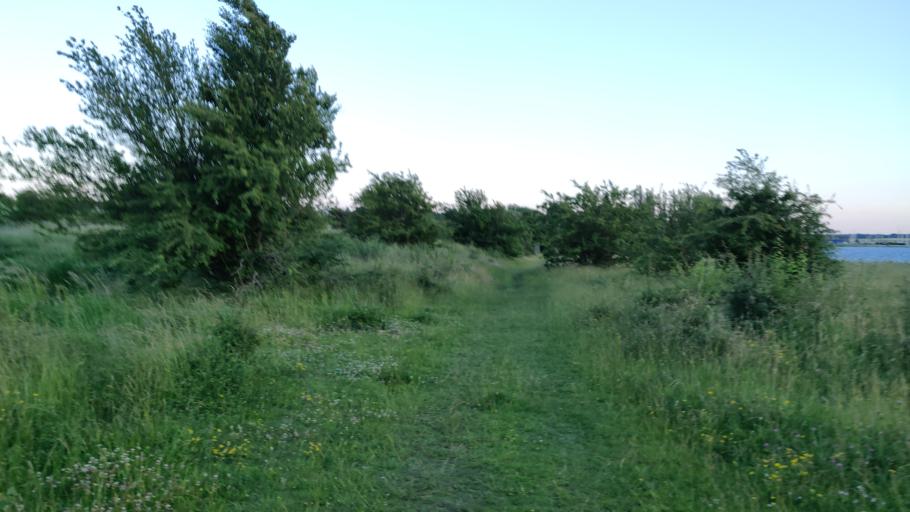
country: DK
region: Zealand
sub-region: Roskilde Kommune
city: Roskilde
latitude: 55.6854
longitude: 12.0763
